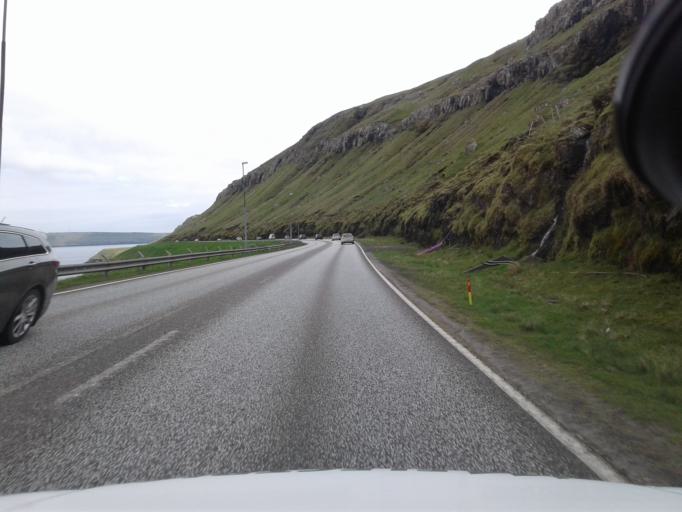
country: FO
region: Streymoy
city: Hoyvik
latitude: 62.0465
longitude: -6.8373
